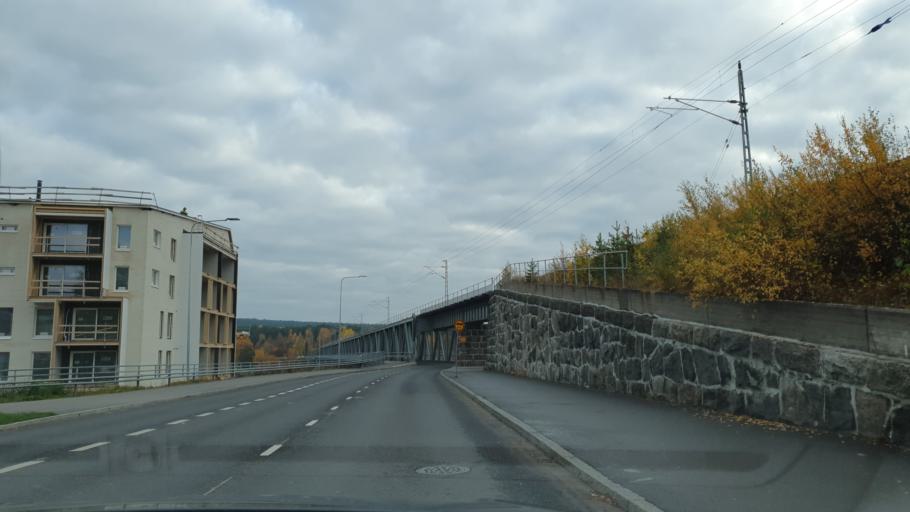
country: FI
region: Lapland
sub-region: Rovaniemi
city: Rovaniemi
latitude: 66.4957
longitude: 25.7319
